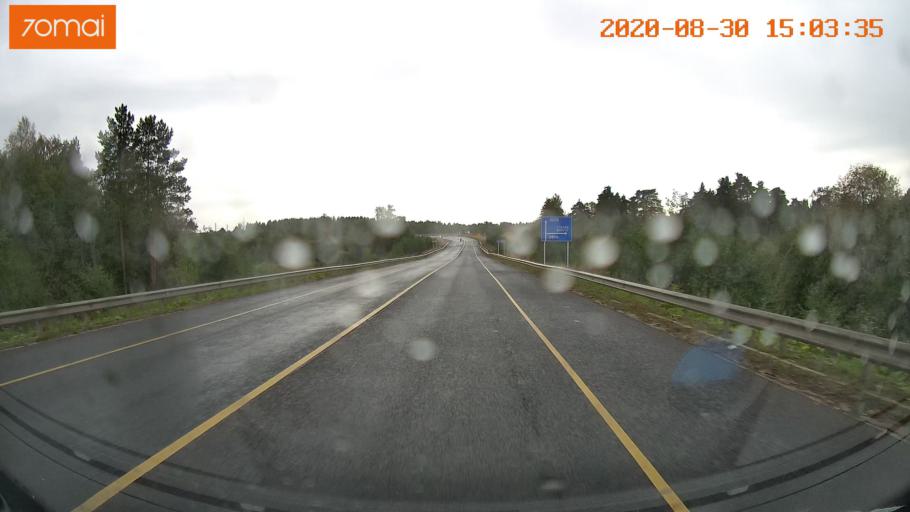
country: RU
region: Ivanovo
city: Staraya Vichuga
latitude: 57.2974
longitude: 41.9105
